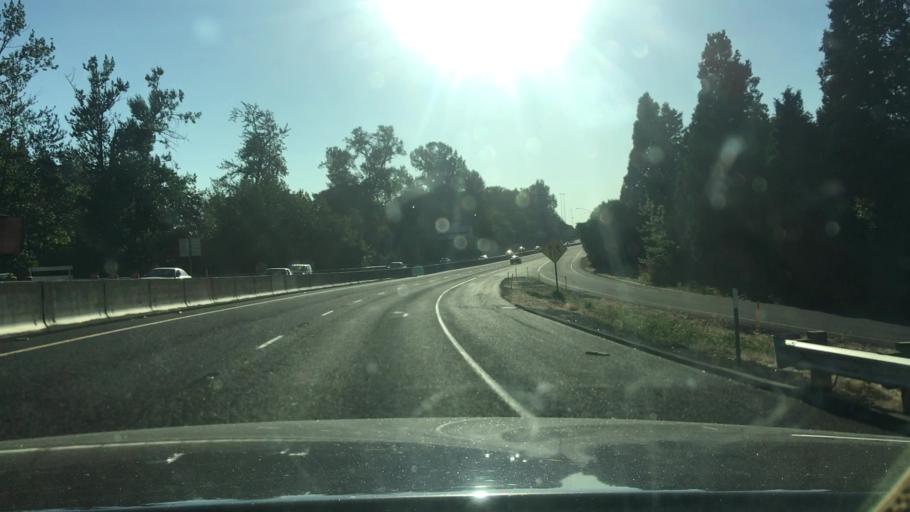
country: US
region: Oregon
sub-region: Lane County
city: Eugene
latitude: 44.0612
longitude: -123.0865
